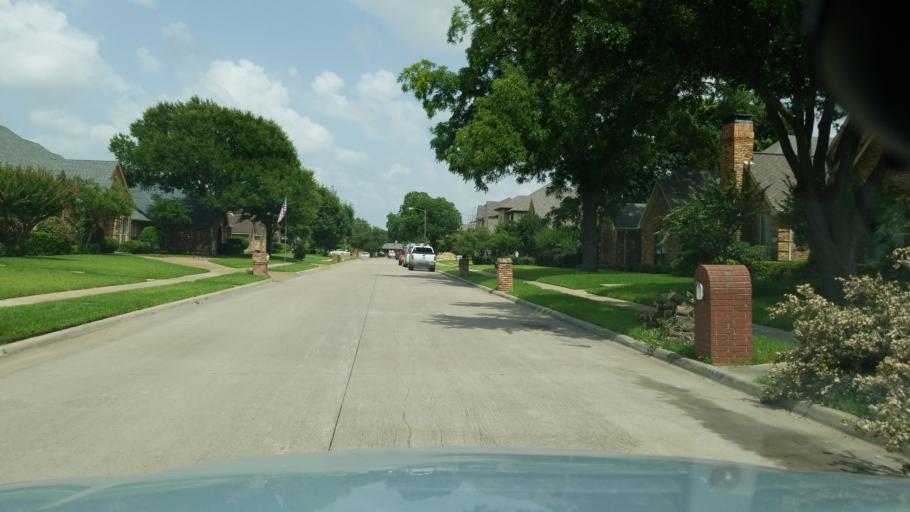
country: US
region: Texas
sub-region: Dallas County
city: Irving
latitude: 32.8191
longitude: -96.9278
